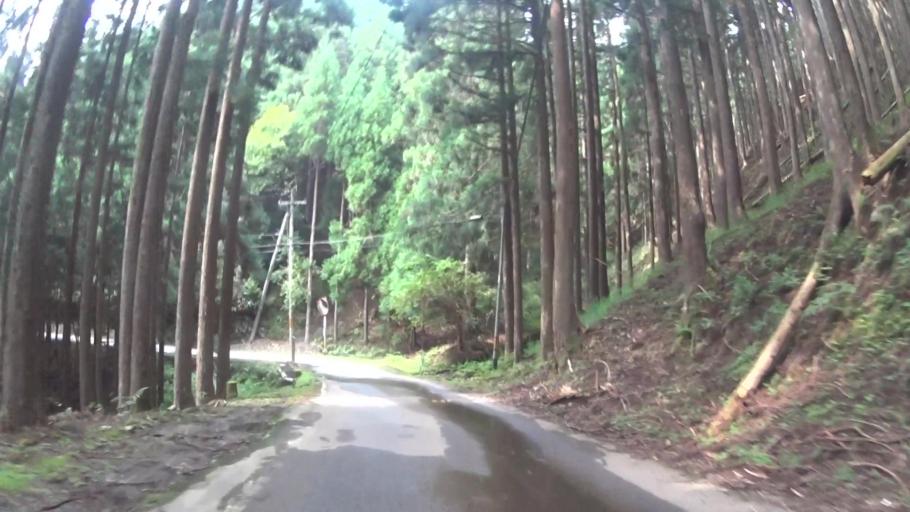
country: JP
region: Kyoto
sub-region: Kyoto-shi
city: Kamigyo-ku
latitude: 35.1792
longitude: 135.7351
